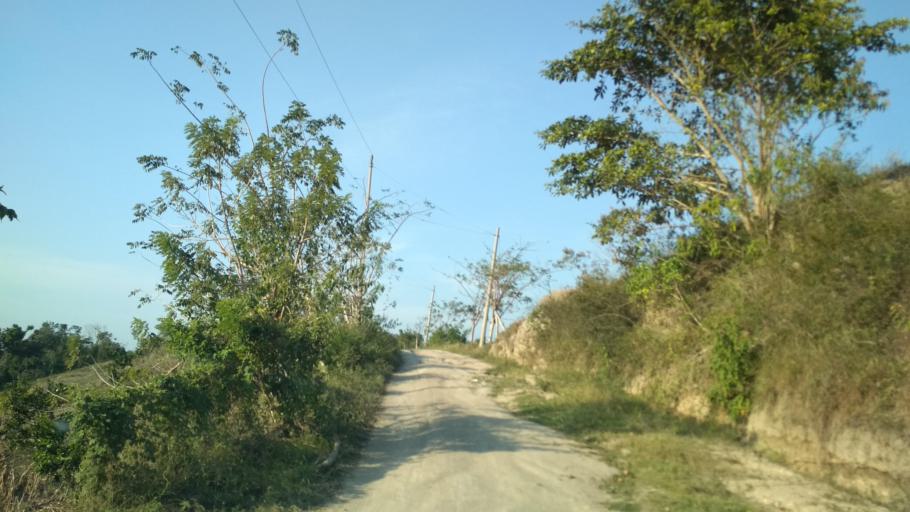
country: MX
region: Puebla
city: San Jose Acateno
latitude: 20.2289
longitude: -97.2566
